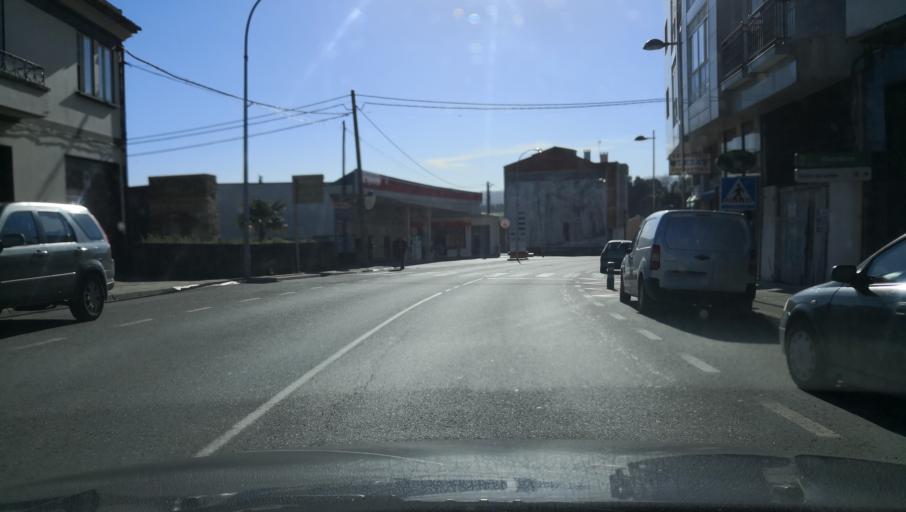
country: ES
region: Galicia
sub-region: Provincia de Pontevedra
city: Silleda
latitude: 42.7288
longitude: -8.3023
